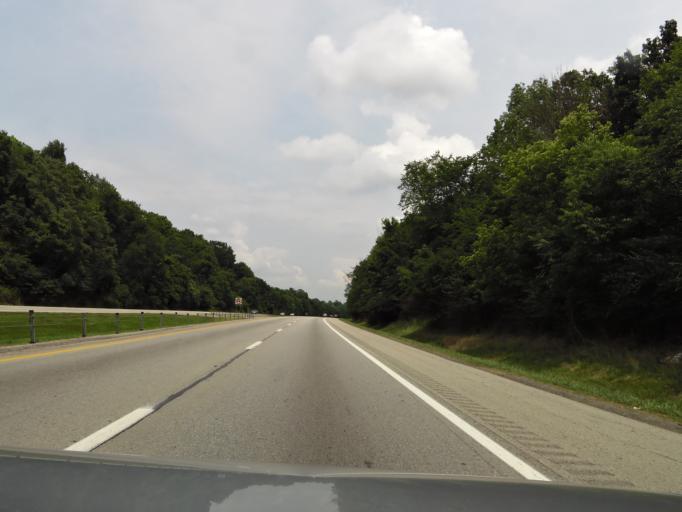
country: US
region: Kentucky
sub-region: Jefferson County
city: Barbourmeade
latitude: 38.2977
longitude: -85.6236
